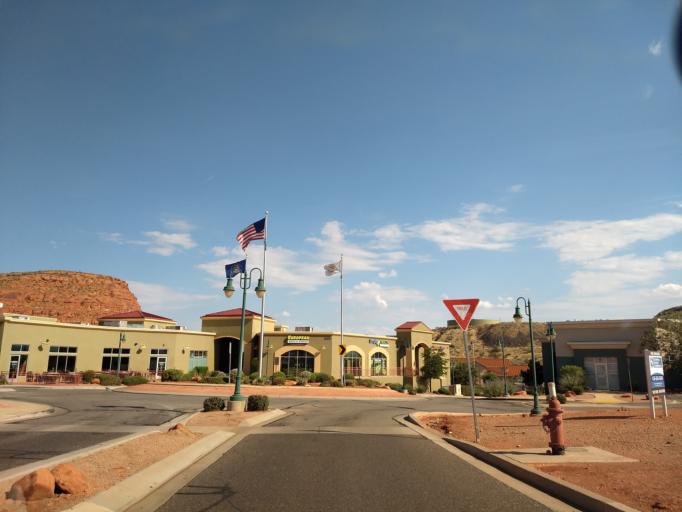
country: US
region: Utah
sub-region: Washington County
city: Saint George
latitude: 37.1263
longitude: -113.6025
